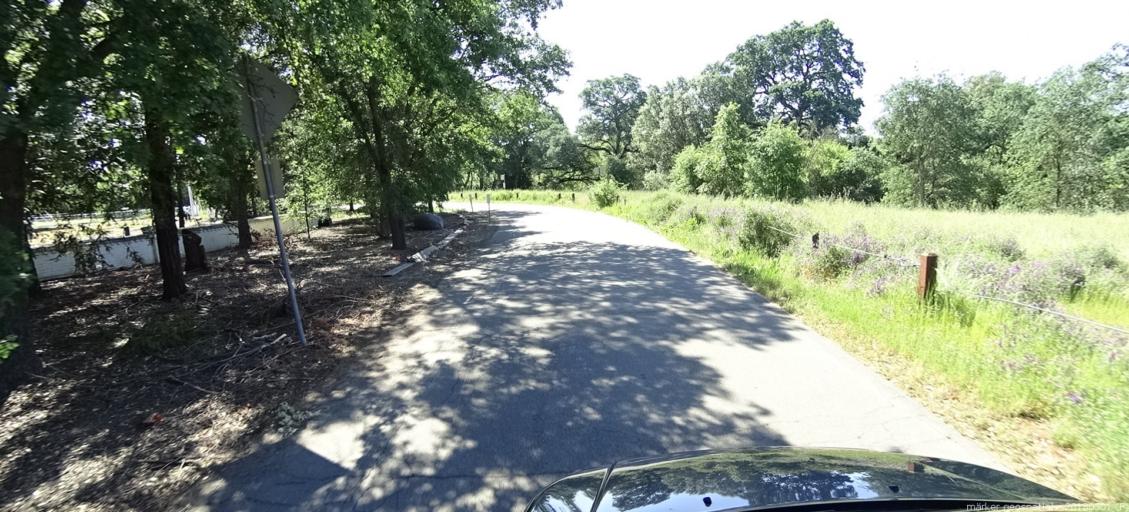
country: US
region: California
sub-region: Sacramento County
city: Foothill Farms
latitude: 38.6439
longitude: -121.3708
